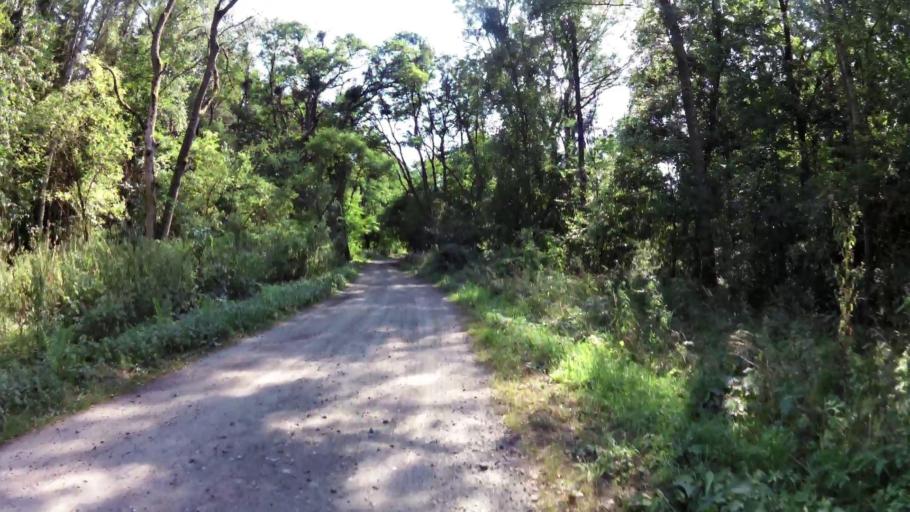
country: PL
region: West Pomeranian Voivodeship
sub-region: Powiat gryfinski
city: Moryn
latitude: 52.8698
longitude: 14.4275
